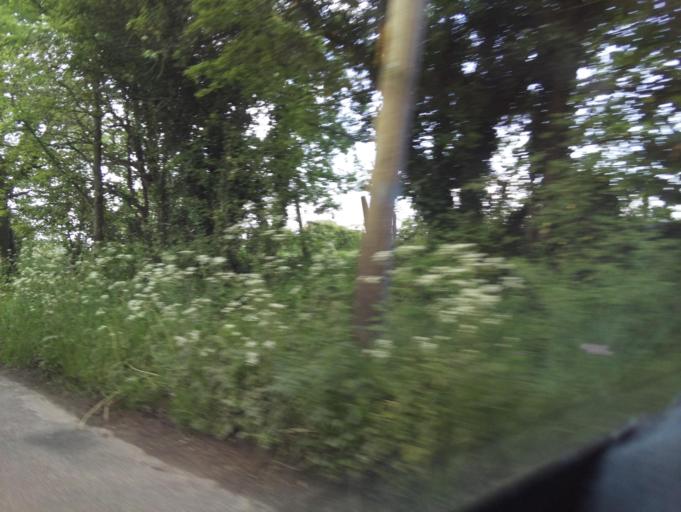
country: GB
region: England
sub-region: Wiltshire
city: Malmesbury
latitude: 51.5438
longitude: -2.0847
